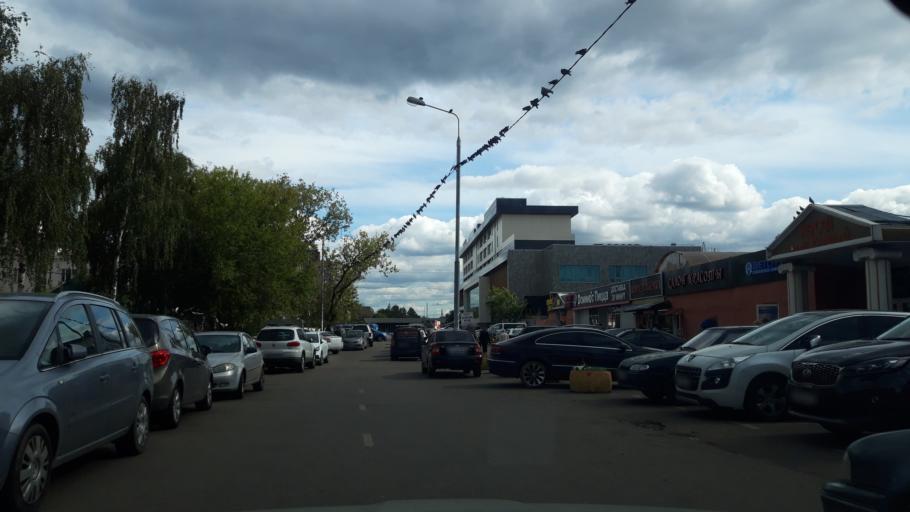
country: RU
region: Moskovskaya
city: Levoberezhnyy
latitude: 55.8424
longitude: 37.4849
